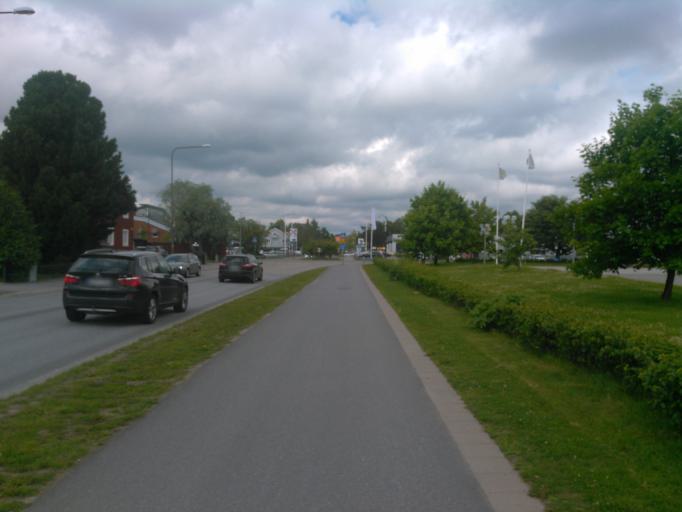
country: SE
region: Vaesterbotten
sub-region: Umea Kommun
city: Umea
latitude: 63.8317
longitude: 20.2828
